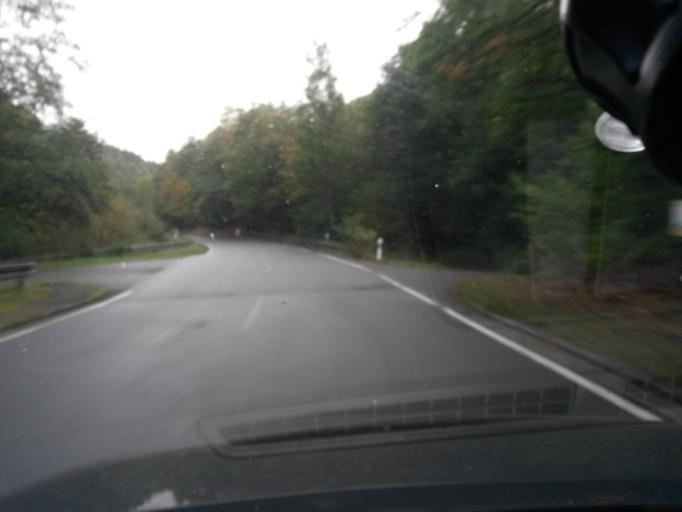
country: DE
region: North Rhine-Westphalia
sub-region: Regierungsbezirk Arnsberg
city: Herscheid
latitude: 51.2106
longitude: 7.7232
